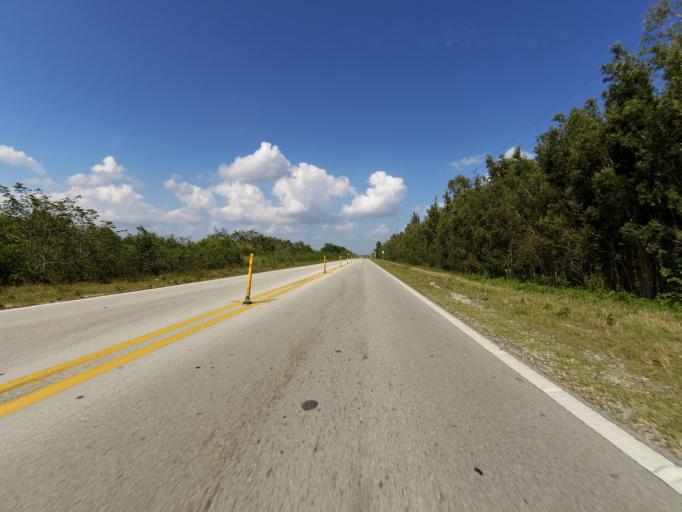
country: US
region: Florida
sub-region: Miami-Dade County
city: Palm Springs North
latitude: 25.9229
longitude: -80.4564
